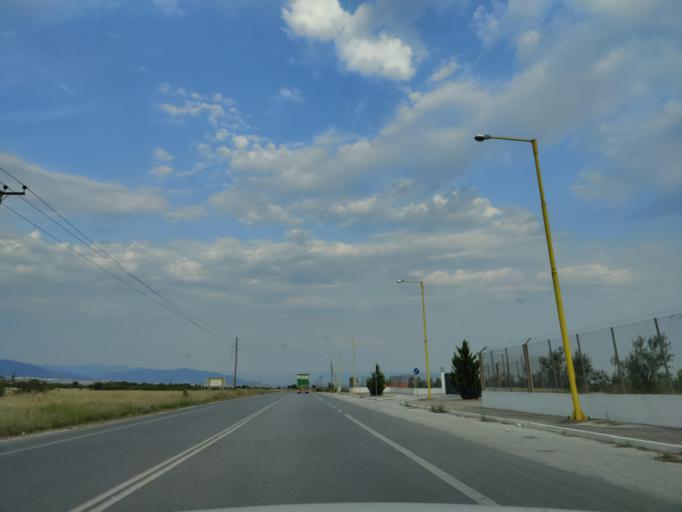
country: GR
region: East Macedonia and Thrace
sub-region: Nomos Dramas
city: Petroussa
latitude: 41.1757
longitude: 24.0102
